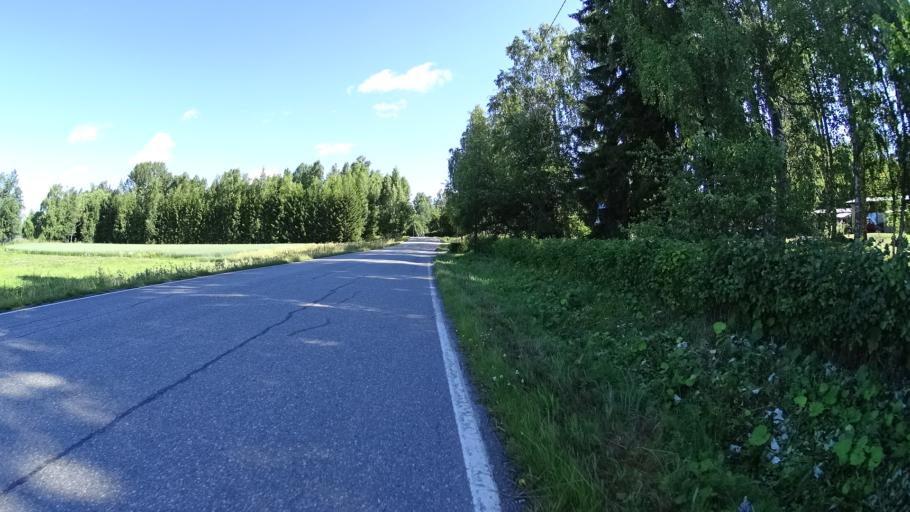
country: FI
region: Uusimaa
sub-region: Helsinki
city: Tuusula
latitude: 60.4348
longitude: 25.0595
